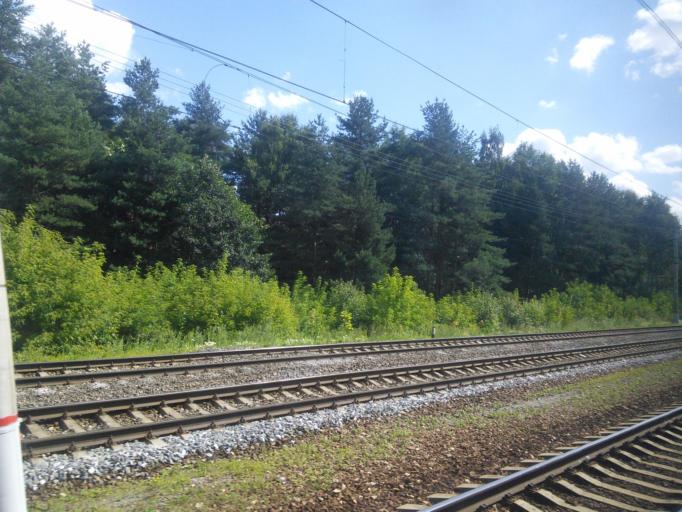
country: RU
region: Moskovskaya
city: Kratovo
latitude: 55.5860
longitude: 38.1749
